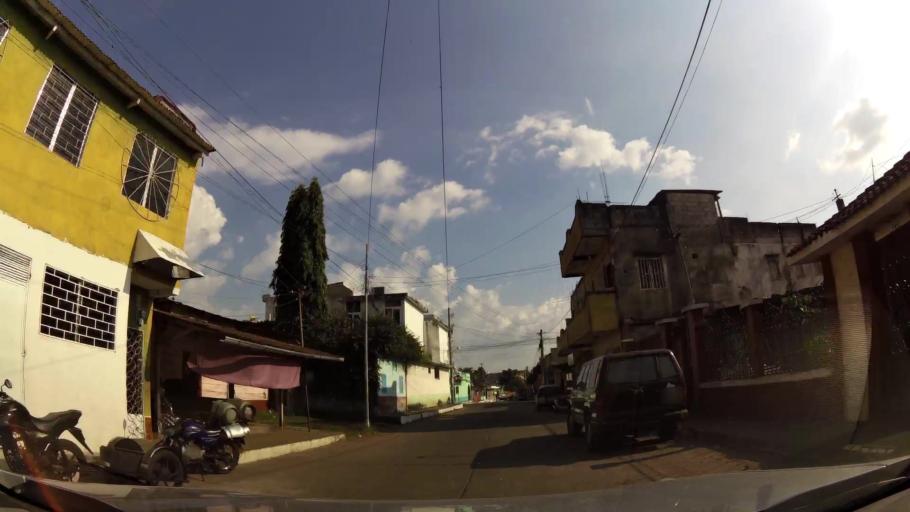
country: GT
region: Retalhuleu
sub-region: Municipio de Retalhuleu
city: Retalhuleu
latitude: 14.5370
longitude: -91.6865
